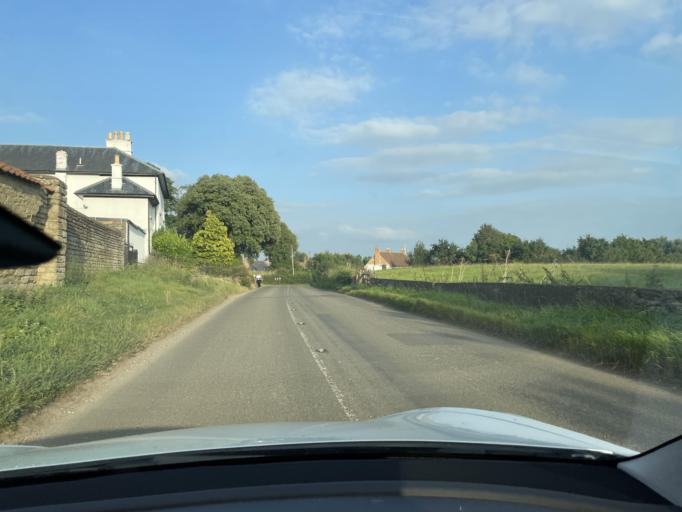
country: GB
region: England
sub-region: Northamptonshire
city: Raunds
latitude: 52.3701
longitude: -0.4517
